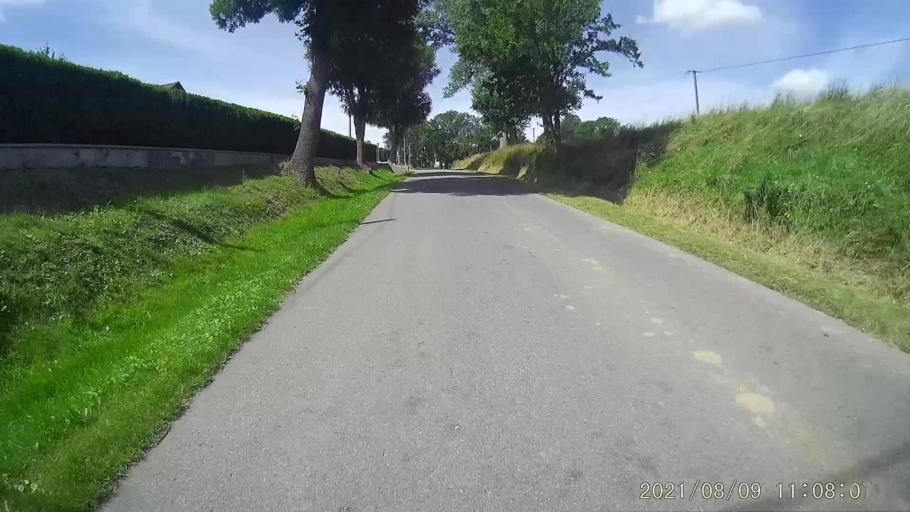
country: PL
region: Lower Silesian Voivodeship
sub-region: Powiat klodzki
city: Klodzko
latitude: 50.4556
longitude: 16.6062
